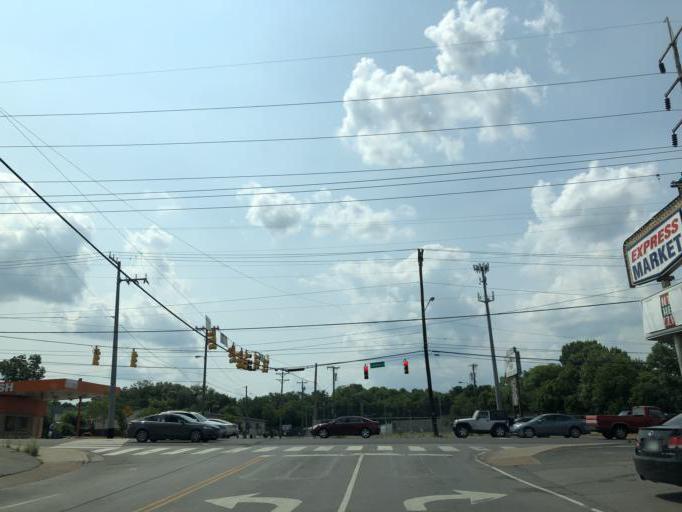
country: US
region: Tennessee
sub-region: Davidson County
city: Goodlettsville
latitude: 36.2518
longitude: -86.7173
